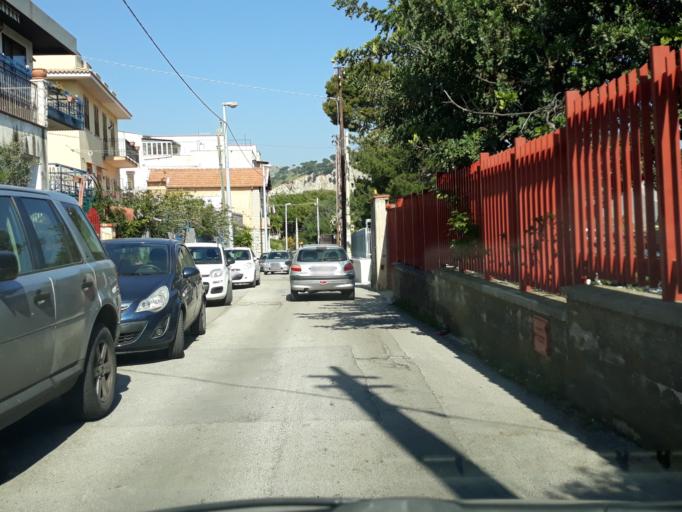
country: IT
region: Sicily
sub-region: Palermo
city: Piano dei Geli
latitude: 38.1121
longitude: 13.2980
